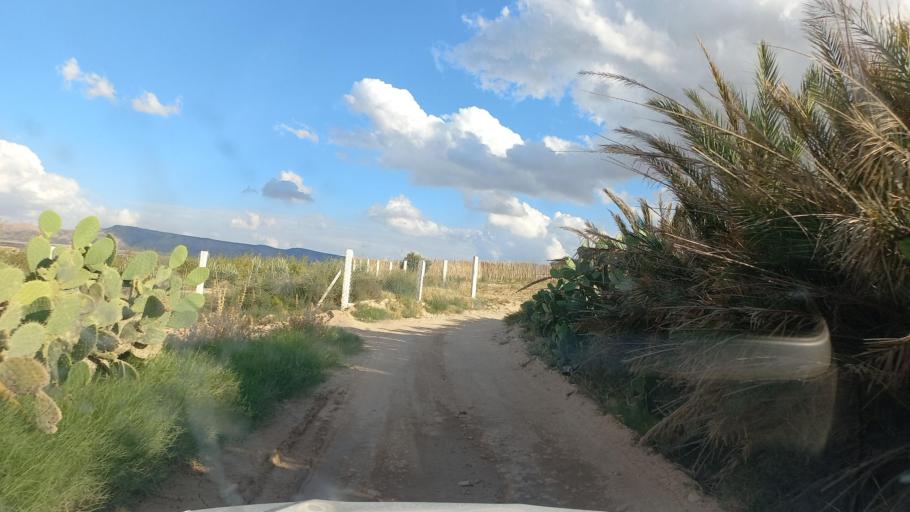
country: TN
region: Al Qasrayn
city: Sbiba
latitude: 35.3795
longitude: 9.0755
